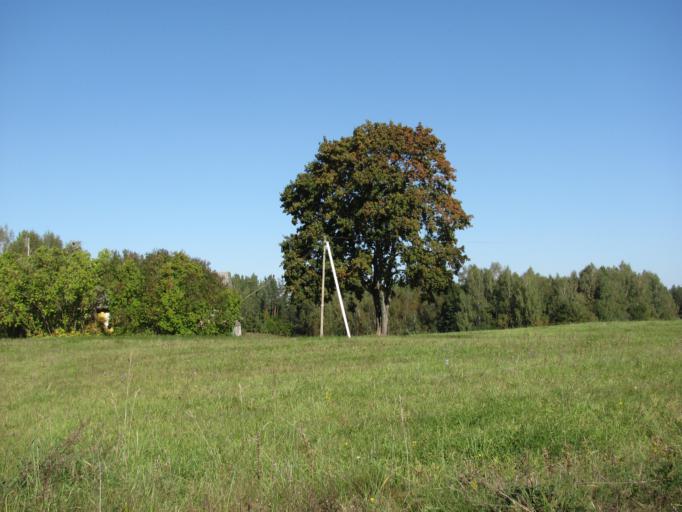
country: LT
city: Zarasai
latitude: 55.6210
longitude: 25.9464
